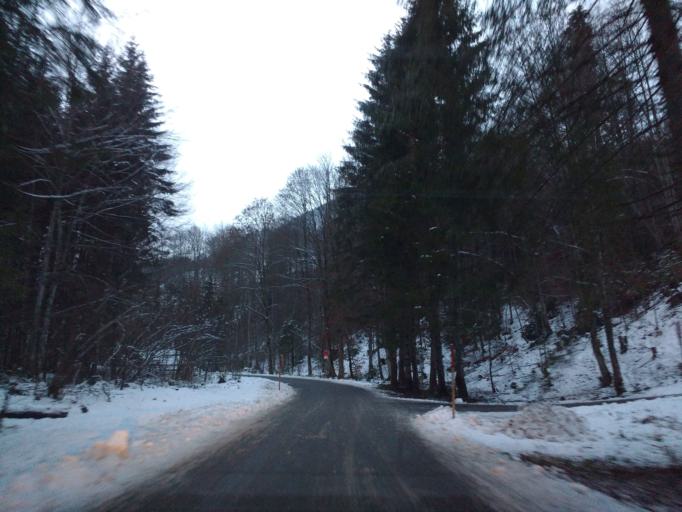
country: DE
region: Bavaria
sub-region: Swabia
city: Obermaiselstein
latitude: 47.4057
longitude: 10.2283
